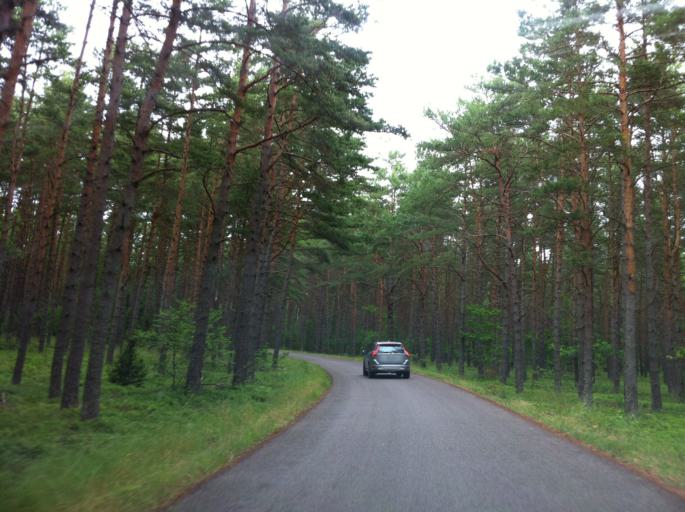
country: SE
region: Kalmar
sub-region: Vasterviks Kommun
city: Vaestervik
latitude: 57.3323
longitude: 17.1057
